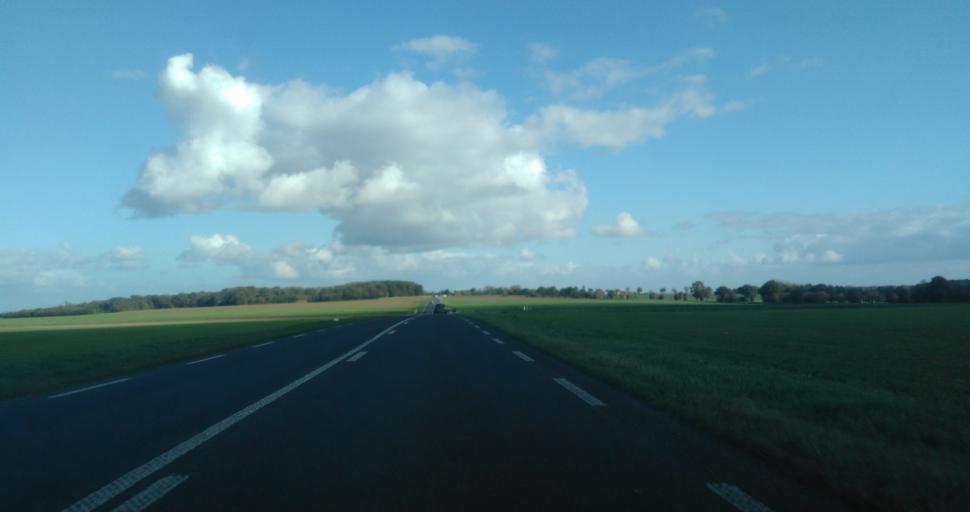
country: FR
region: Nord-Pas-de-Calais
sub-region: Departement du Pas-de-Calais
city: Beaumetz-les-Loges
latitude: 50.2314
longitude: 2.6304
